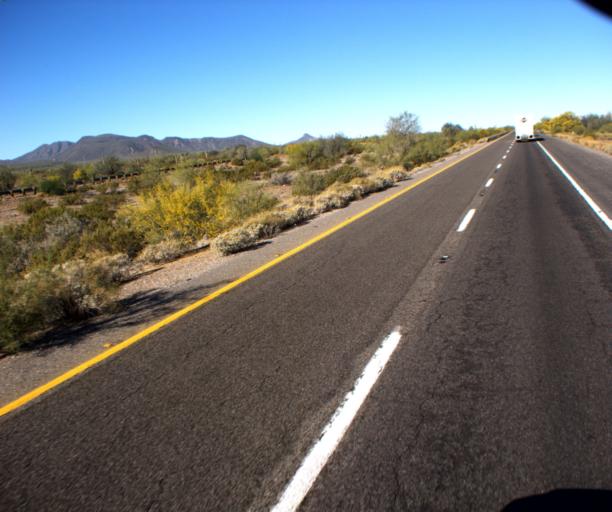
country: US
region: Arizona
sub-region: Pinal County
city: Maricopa
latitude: 32.8314
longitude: -112.0452
